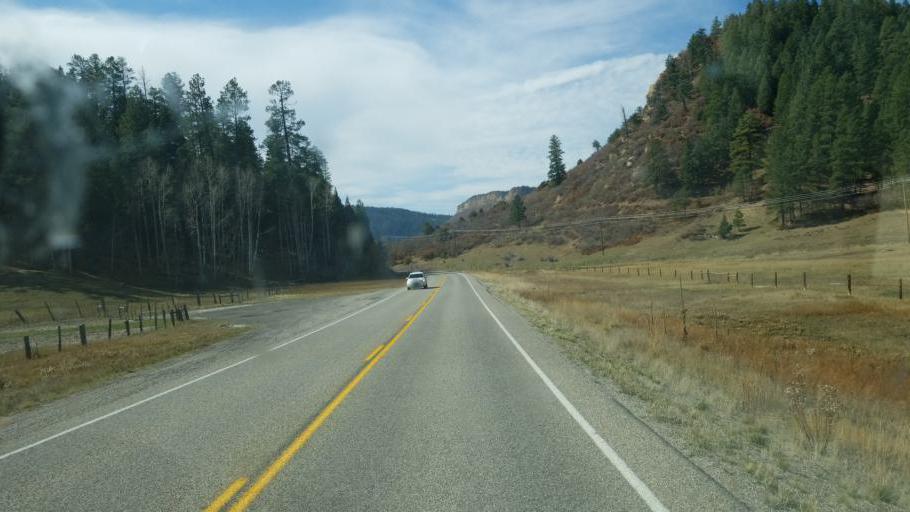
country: US
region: New Mexico
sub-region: Rio Arriba County
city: Dulce
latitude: 37.0701
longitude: -106.8269
